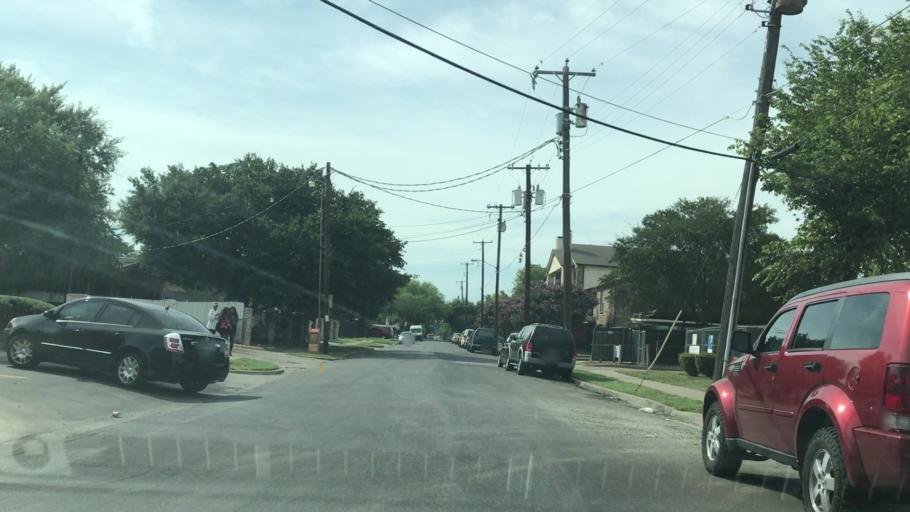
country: US
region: Texas
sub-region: Dallas County
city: Highland Park
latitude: 32.8082
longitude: -96.7746
